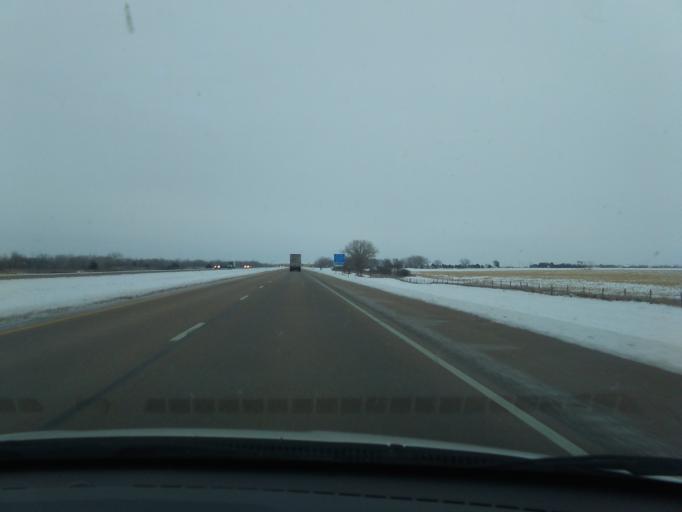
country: US
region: Nebraska
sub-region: Keith County
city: Ogallala
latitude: 41.1040
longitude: -101.7675
